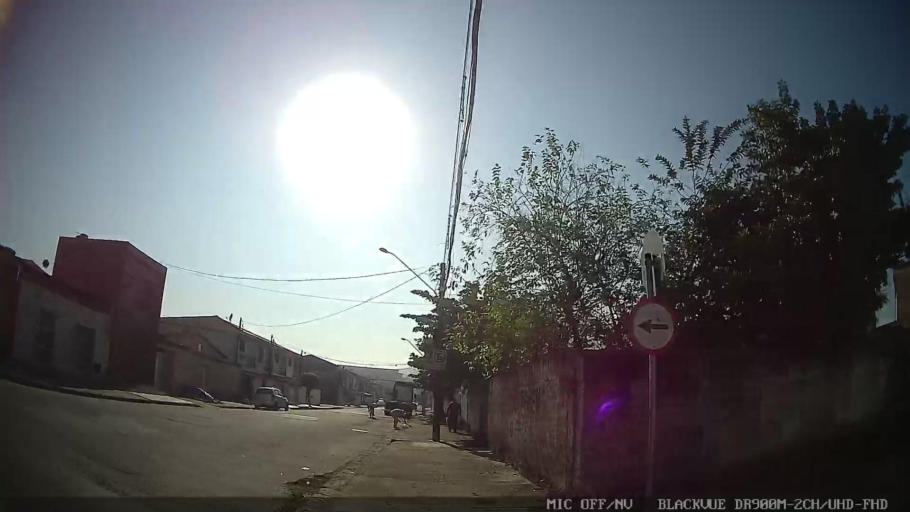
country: BR
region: Sao Paulo
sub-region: Guaruja
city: Guaruja
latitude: -23.9864
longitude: -46.2705
